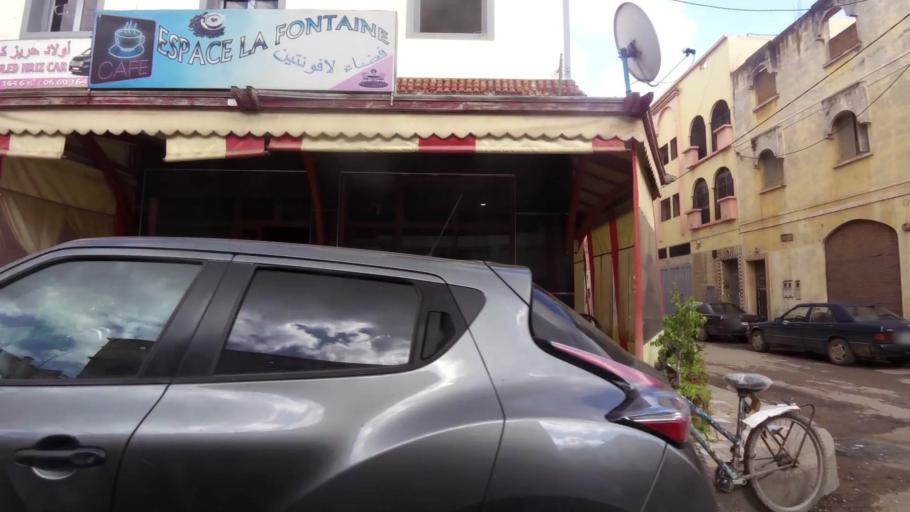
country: MA
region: Chaouia-Ouardigha
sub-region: Settat Province
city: Berrechid
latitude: 33.2664
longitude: -7.5766
